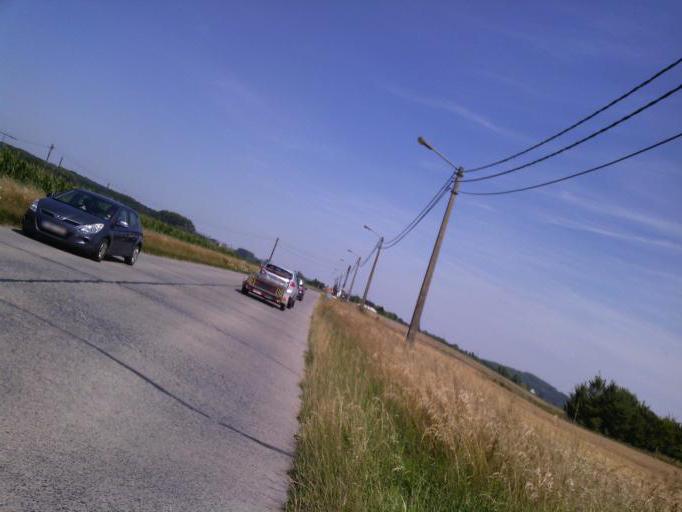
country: BE
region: Wallonia
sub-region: Province du Hainaut
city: Tournai
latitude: 50.6149
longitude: 3.4369
